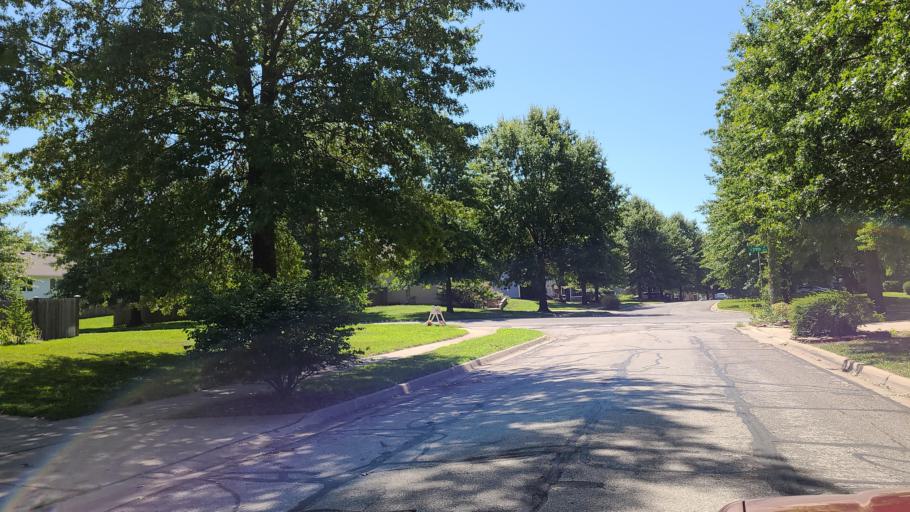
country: US
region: Kansas
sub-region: Douglas County
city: Lawrence
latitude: 38.9320
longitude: -95.2085
